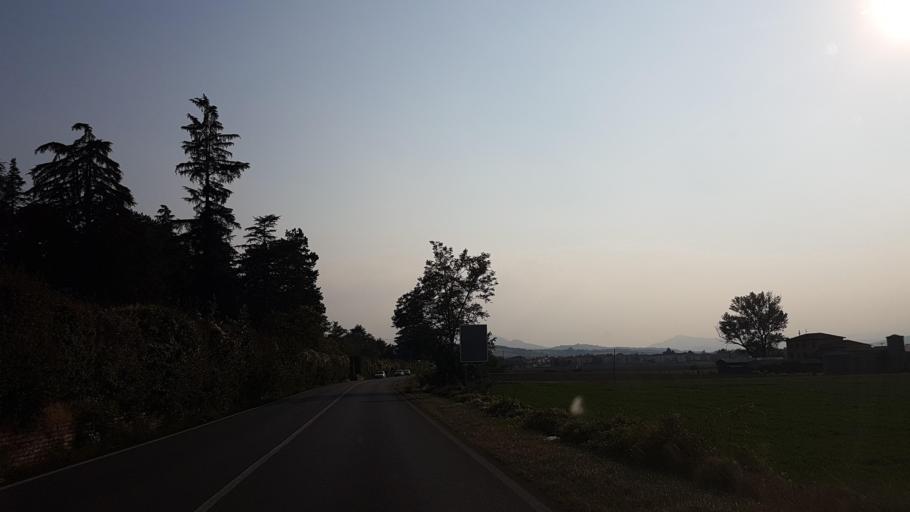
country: IT
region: Emilia-Romagna
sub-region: Provincia di Parma
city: Gaiano
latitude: 44.7312
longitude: 10.1838
